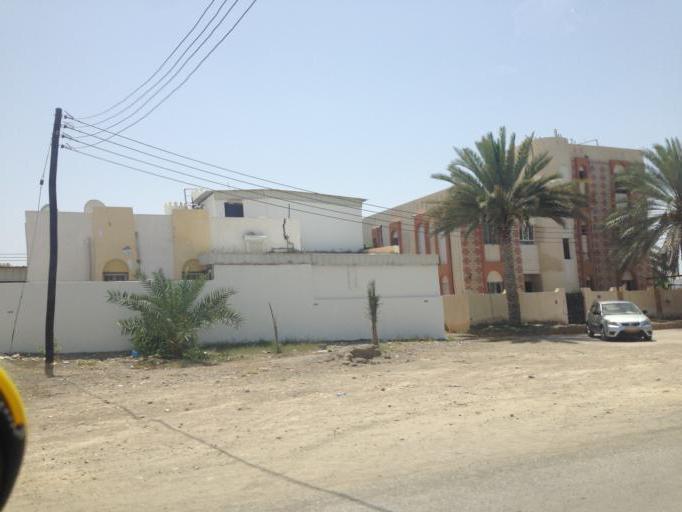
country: OM
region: Muhafazat Masqat
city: As Sib al Jadidah
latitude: 23.6843
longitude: 58.1189
